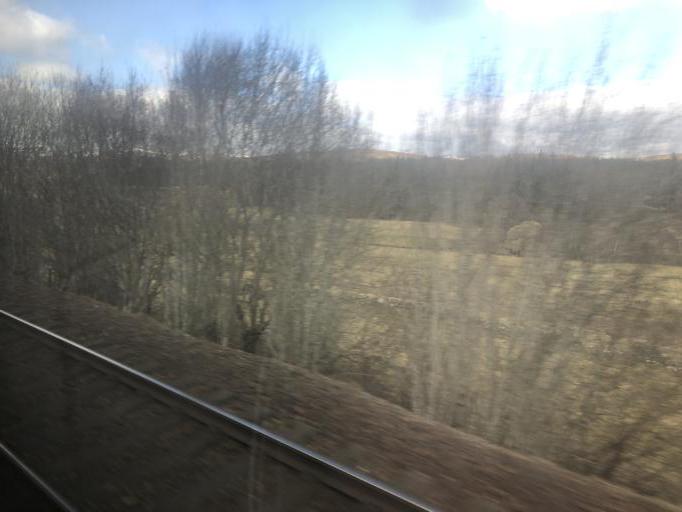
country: GB
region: Scotland
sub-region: Perth and Kinross
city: Aberfeldy
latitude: 56.7979
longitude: -4.0452
